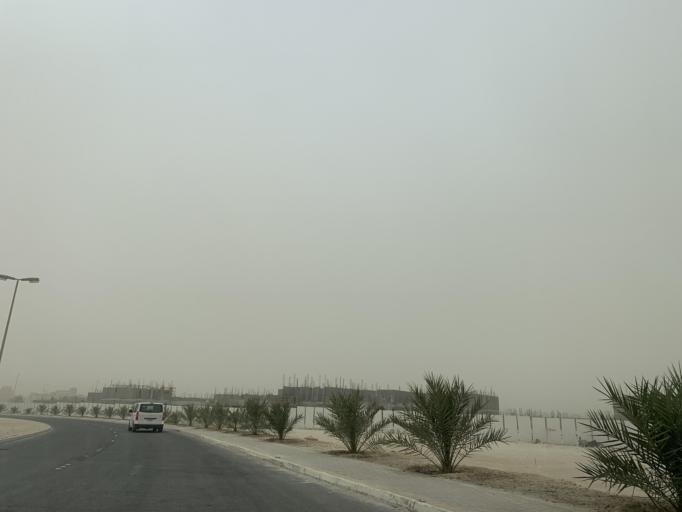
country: BH
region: Central Governorate
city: Madinat Hamad
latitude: 26.1222
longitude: 50.5103
